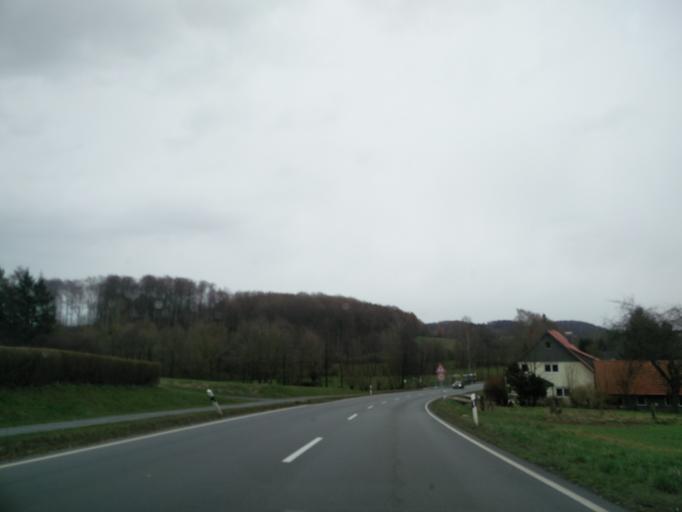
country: DE
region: North Rhine-Westphalia
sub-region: Regierungsbezirk Detmold
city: Horn
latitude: 51.8576
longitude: 8.9591
